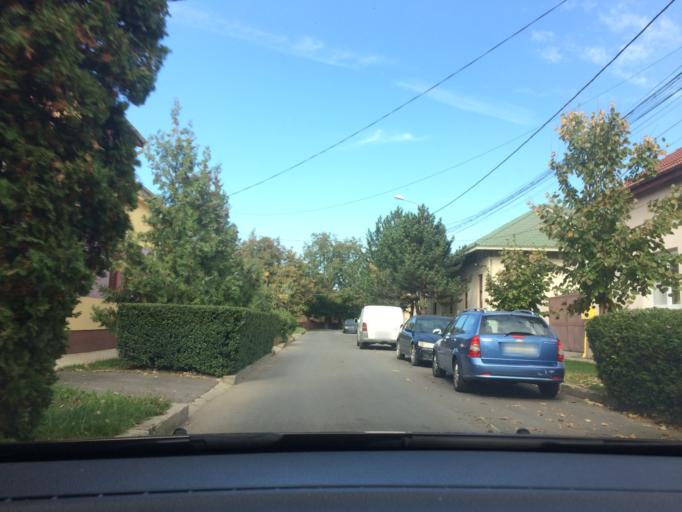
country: RO
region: Timis
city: Timisoara
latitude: 45.7546
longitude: 21.2021
